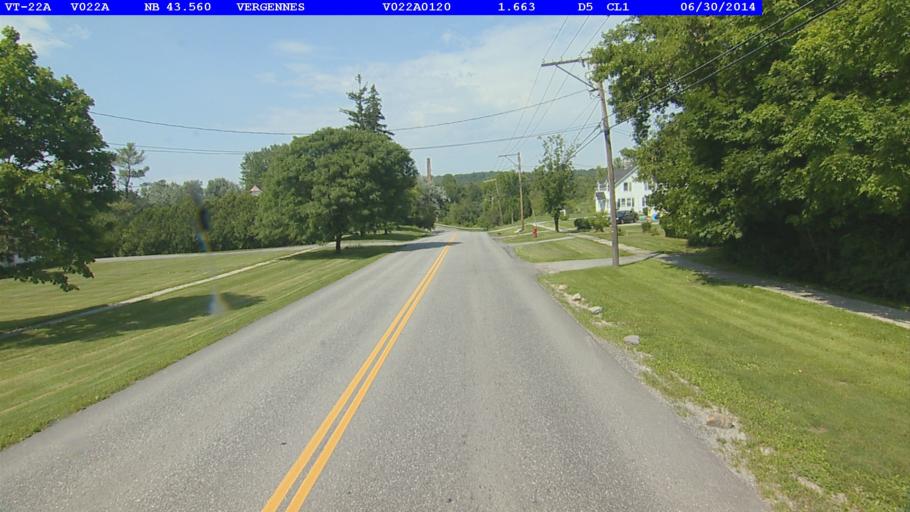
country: US
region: Vermont
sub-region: Addison County
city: Vergennes
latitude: 44.1730
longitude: -73.2471
